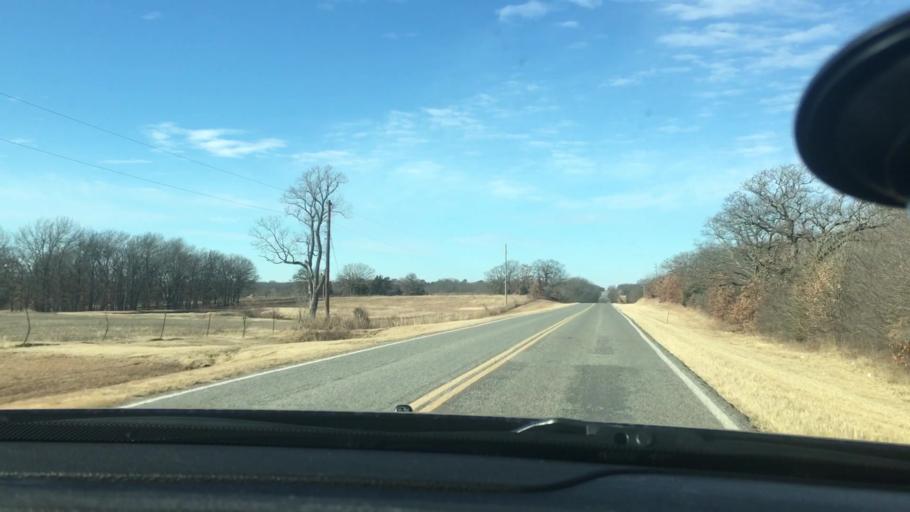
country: US
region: Oklahoma
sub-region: Seminole County
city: Konawa
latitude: 34.9857
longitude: -96.8587
